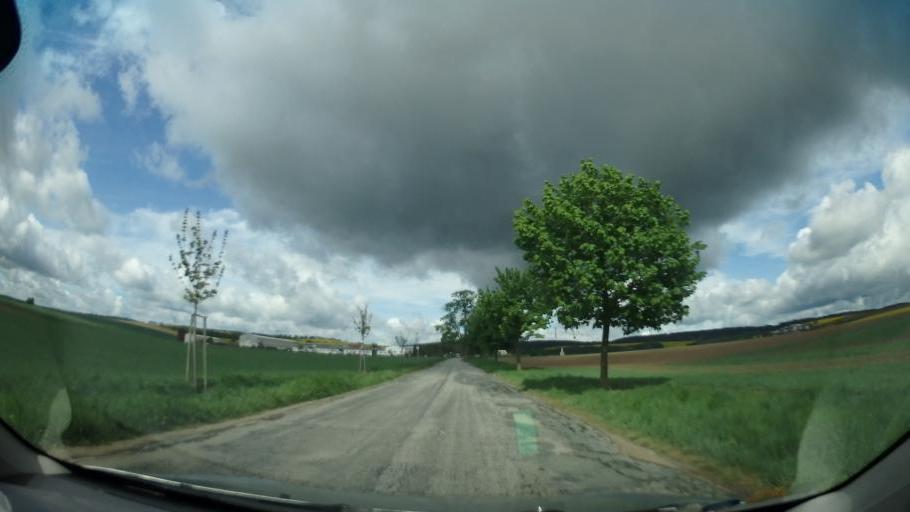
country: CZ
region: South Moravian
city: Ricany
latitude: 49.2286
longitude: 16.4147
